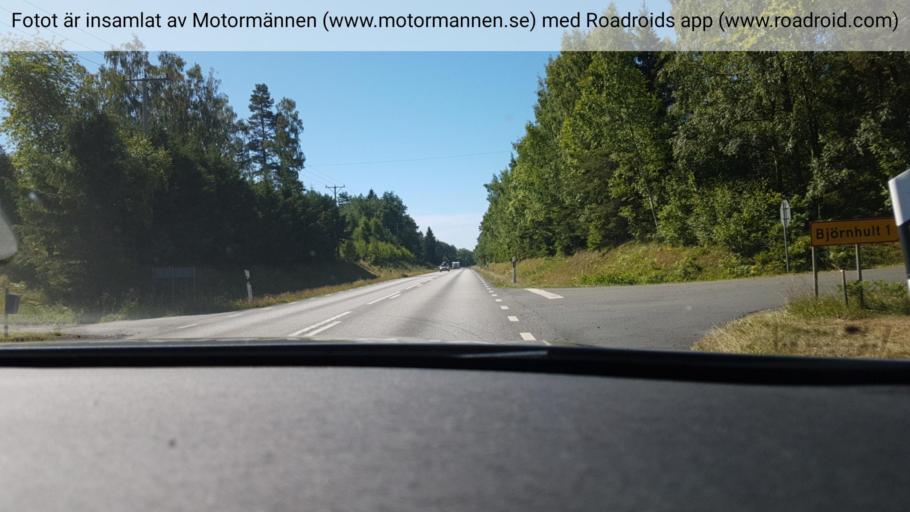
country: SE
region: Joenkoeping
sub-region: Habo Kommun
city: Habo
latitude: 58.0754
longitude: 14.1946
